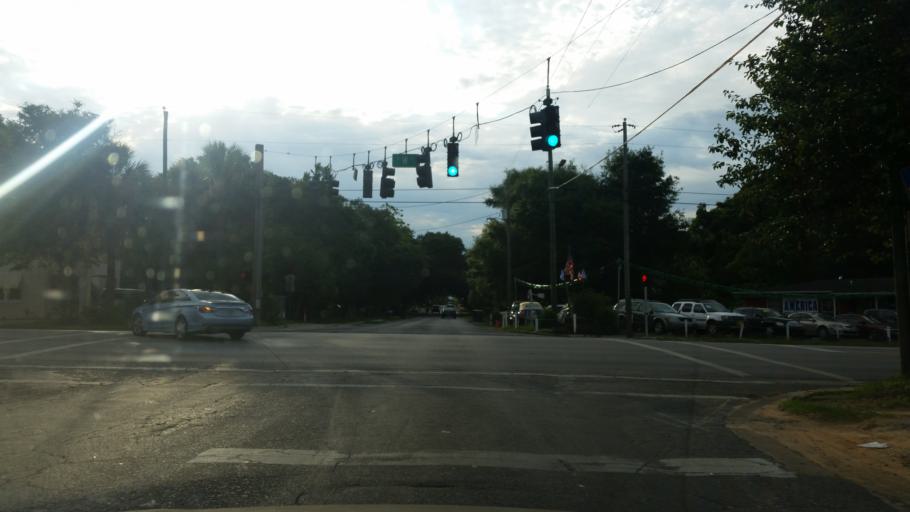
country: US
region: Florida
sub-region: Escambia County
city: West Pensacola
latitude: 30.4191
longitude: -87.2506
